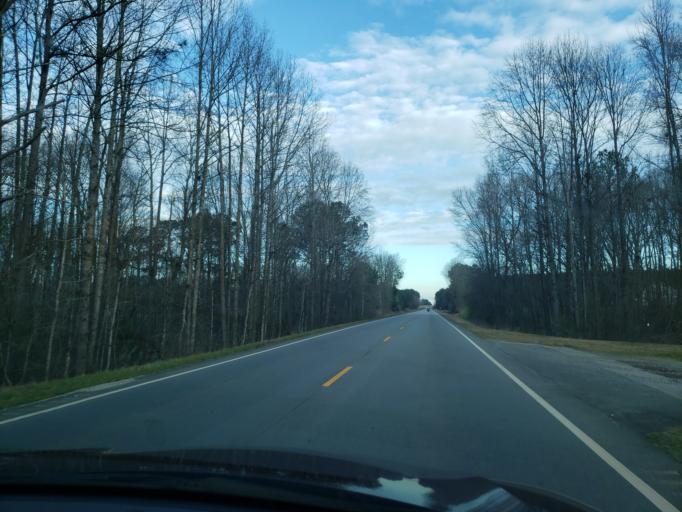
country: US
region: Alabama
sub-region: Randolph County
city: Wedowee
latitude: 33.2652
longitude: -85.4575
